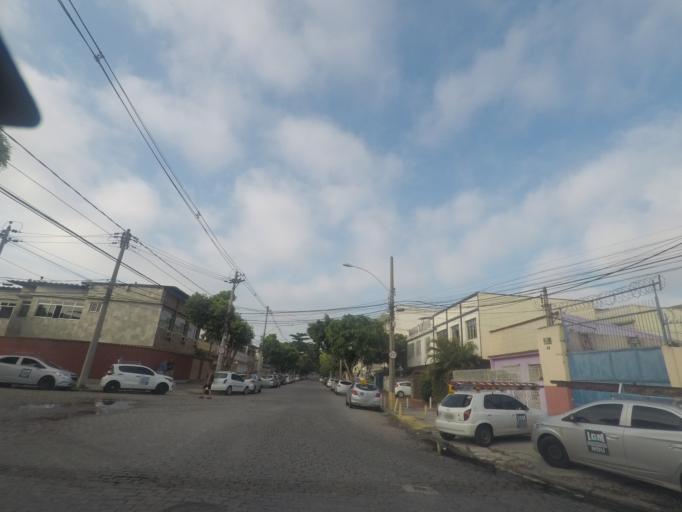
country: BR
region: Rio de Janeiro
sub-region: Duque De Caxias
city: Duque de Caxias
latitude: -22.8374
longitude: -43.2643
